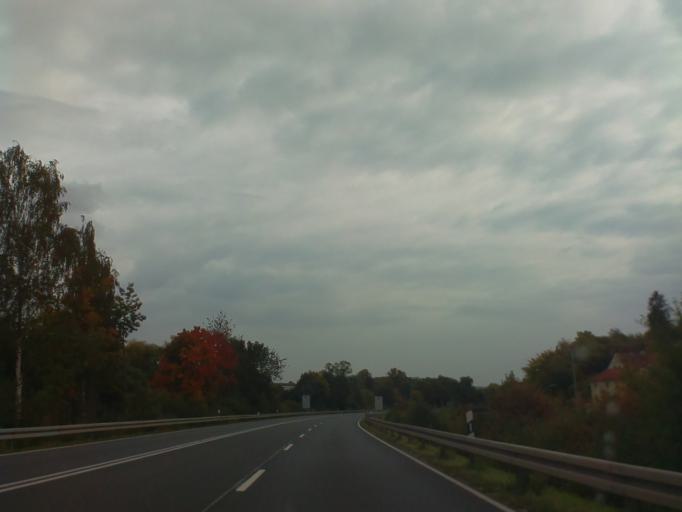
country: DE
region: Hesse
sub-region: Regierungsbezirk Kassel
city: Hunfeld
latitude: 50.6788
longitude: 9.7554
